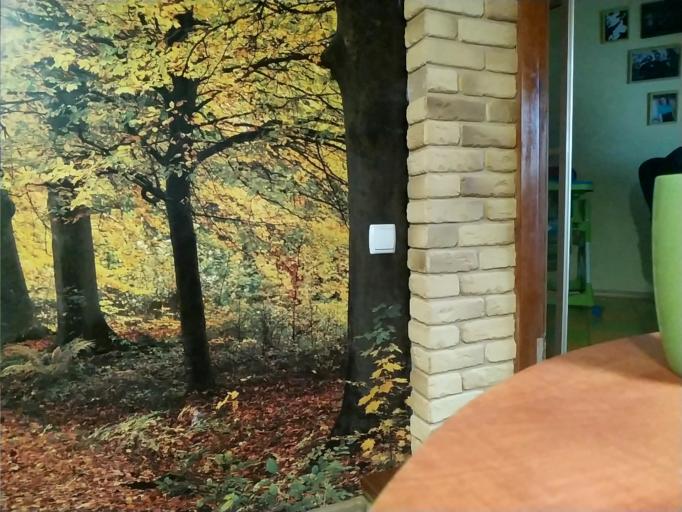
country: RU
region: Tverskaya
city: Staraya Toropa
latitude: 56.3465
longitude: 31.8301
